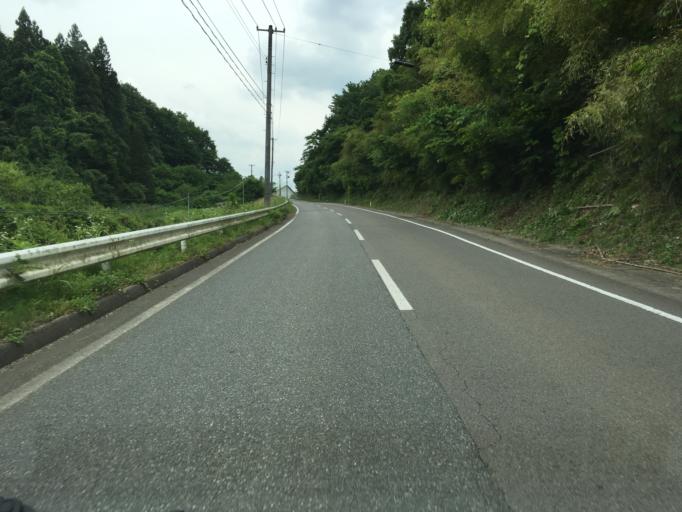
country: JP
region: Fukushima
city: Yanagawamachi-saiwaicho
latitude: 37.7458
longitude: 140.6391
